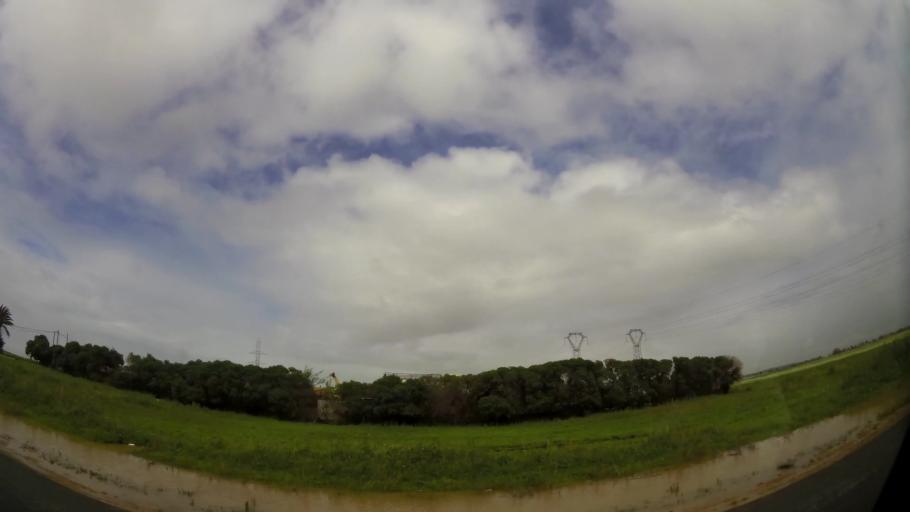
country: MA
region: Grand Casablanca
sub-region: Mohammedia
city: Mohammedia
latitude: 33.6529
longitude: -7.4594
